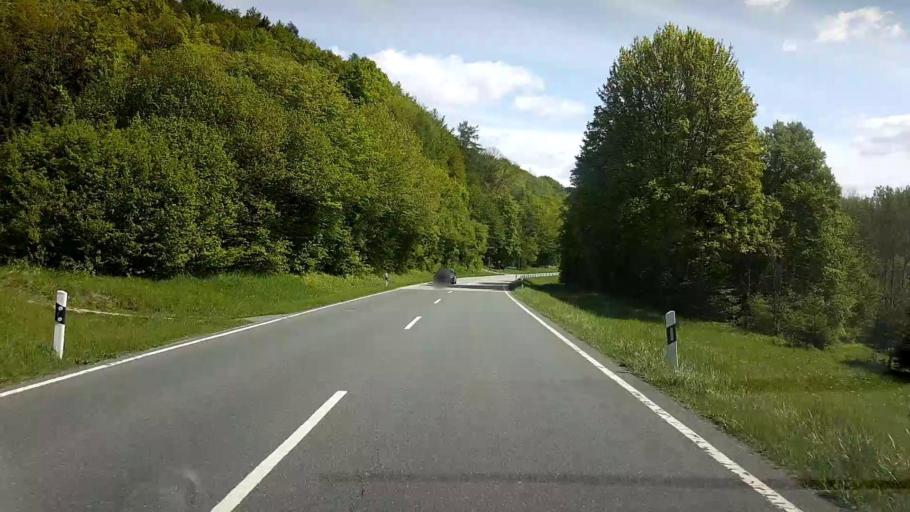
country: DE
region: Bavaria
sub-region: Upper Franconia
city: Ebermannstadt
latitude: 49.7963
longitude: 11.1755
